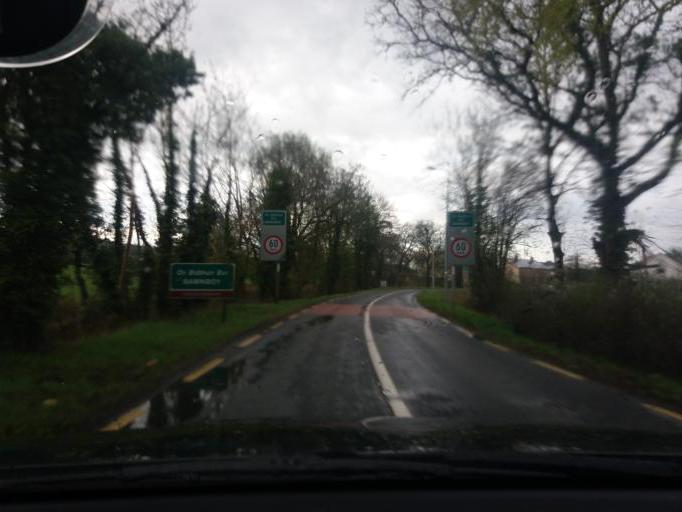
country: IE
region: Ulster
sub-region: An Cabhan
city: Ballyconnell
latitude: 54.1250
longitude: -7.6797
